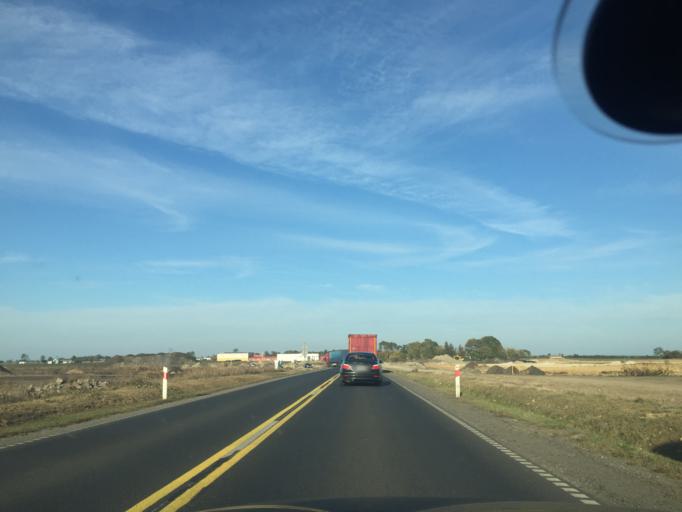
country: PL
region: Kujawsko-Pomorskie
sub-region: Powiat inowroclawski
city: Inowroclaw
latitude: 52.8170
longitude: 18.2917
